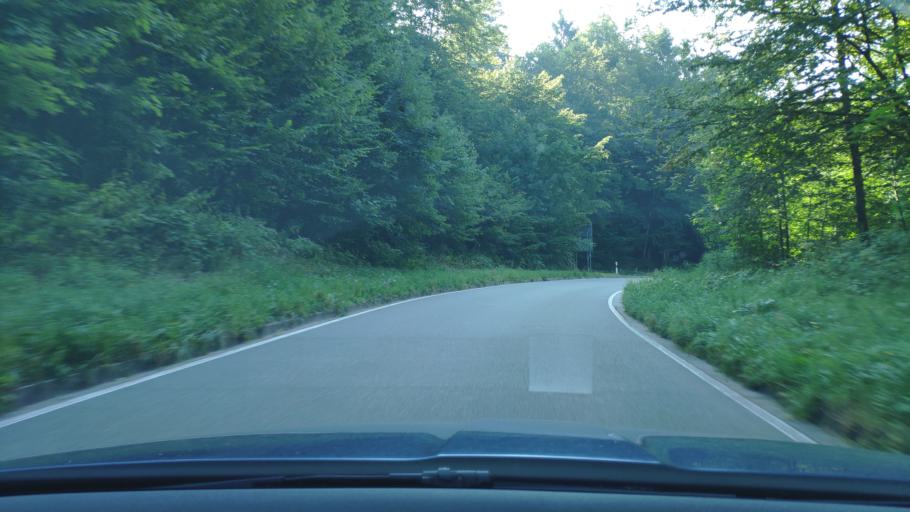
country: DE
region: Rheinland-Pfalz
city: Fischbach
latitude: 49.0661
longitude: 7.7171
